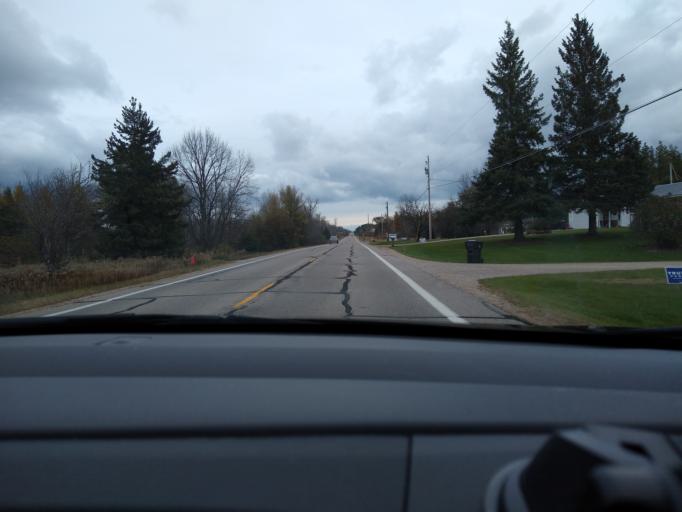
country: US
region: Michigan
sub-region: Delta County
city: Escanaba
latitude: 45.7559
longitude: -87.2906
